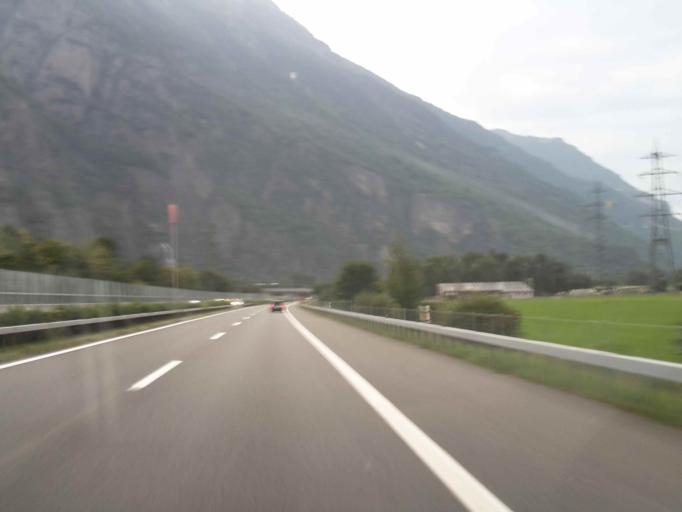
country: CH
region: Valais
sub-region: Saint-Maurice District
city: Vernayaz
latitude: 46.1377
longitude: 7.0464
